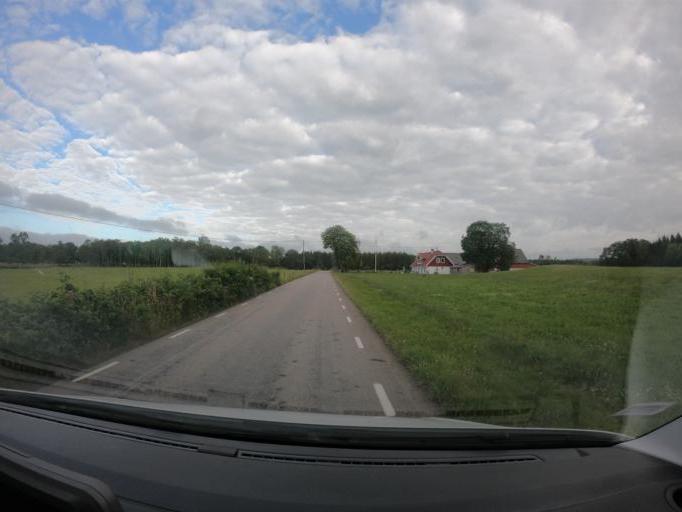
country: SE
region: Skane
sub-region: Angelholms Kommun
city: Munka-Ljungby
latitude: 56.3129
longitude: 13.0221
